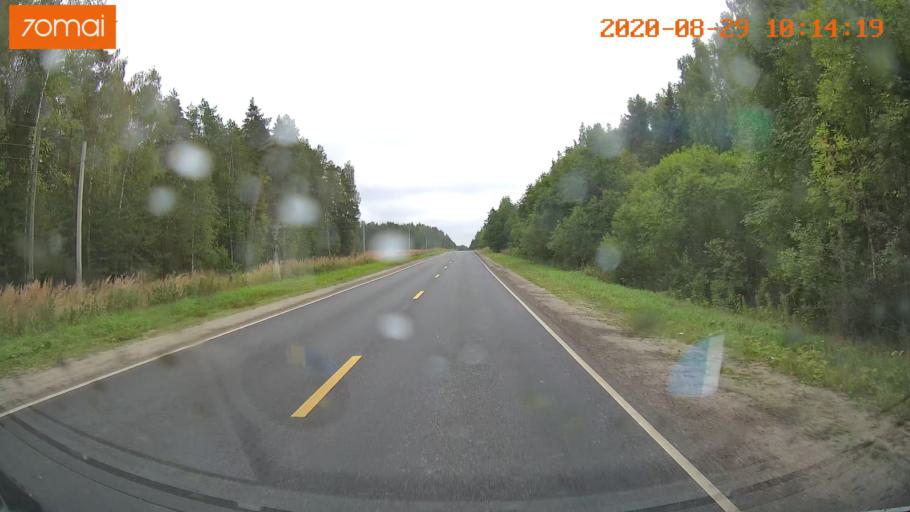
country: RU
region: Ivanovo
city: Yur'yevets
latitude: 57.3539
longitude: 42.7509
